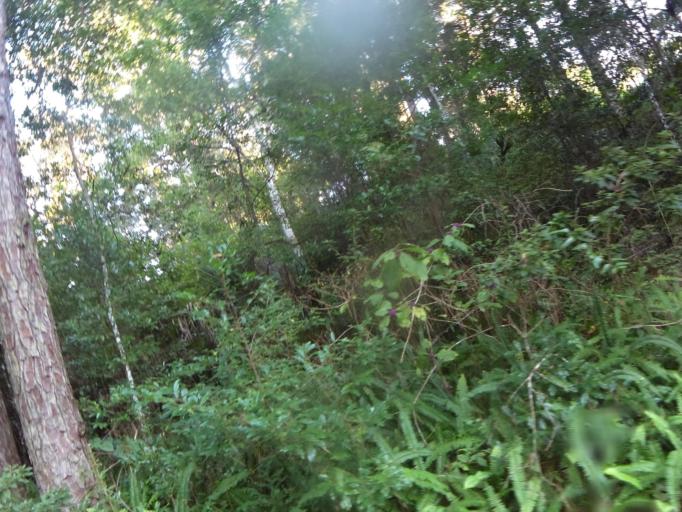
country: US
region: Florida
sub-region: Putnam County
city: Palatka
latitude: 29.6343
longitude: -81.6440
